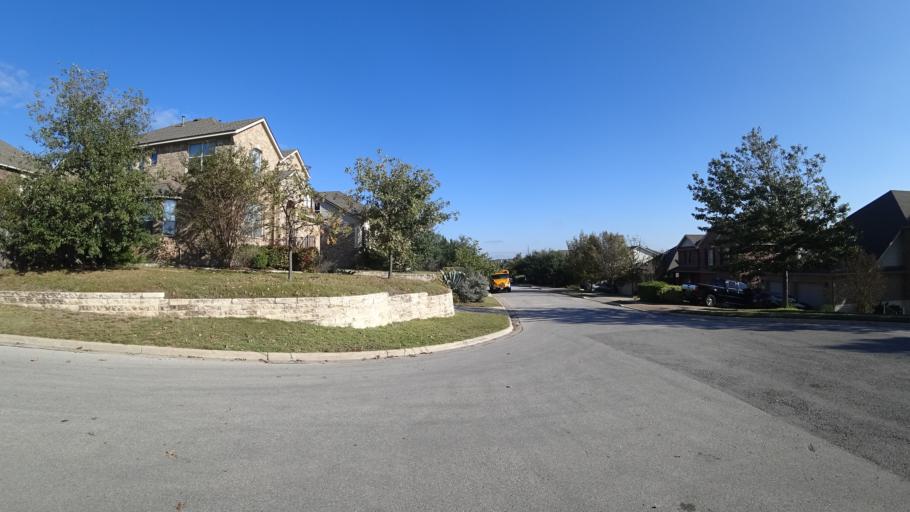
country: US
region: Texas
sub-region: Travis County
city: Hudson Bend
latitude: 30.3651
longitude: -97.8976
